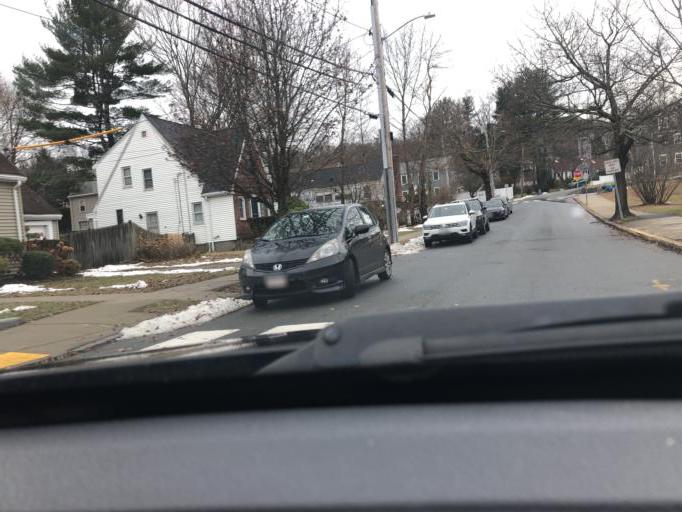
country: US
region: Massachusetts
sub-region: Middlesex County
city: Arlington
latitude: 42.4240
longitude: -71.1549
